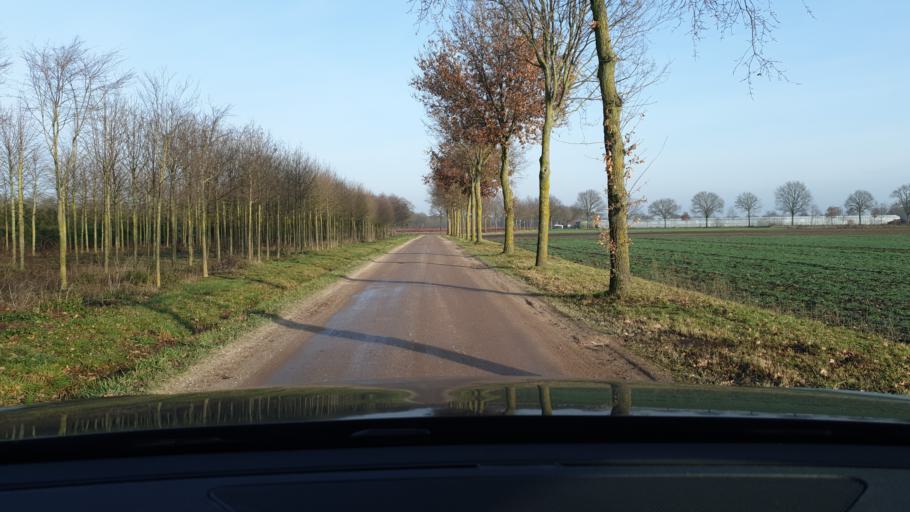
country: NL
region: Limburg
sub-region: Gemeente Peel en Maas
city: Maasbree
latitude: 51.4278
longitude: 6.0616
